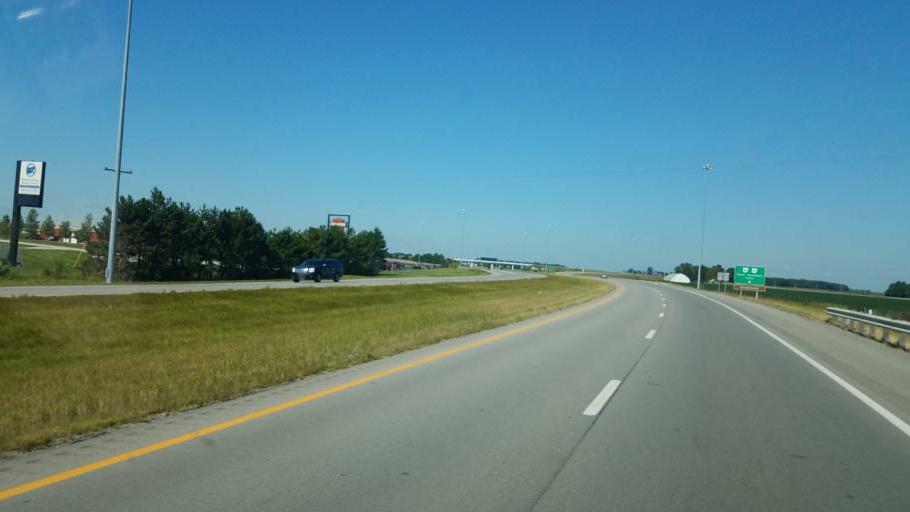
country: US
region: Ohio
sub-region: Wyandot County
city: Upper Sandusky
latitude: 40.8578
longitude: -83.2711
